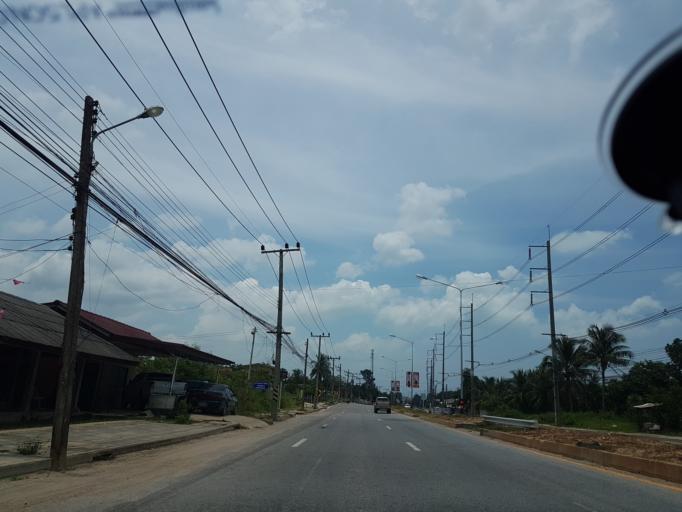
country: TH
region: Songkhla
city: Songkhla
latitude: 7.1143
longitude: 100.6326
